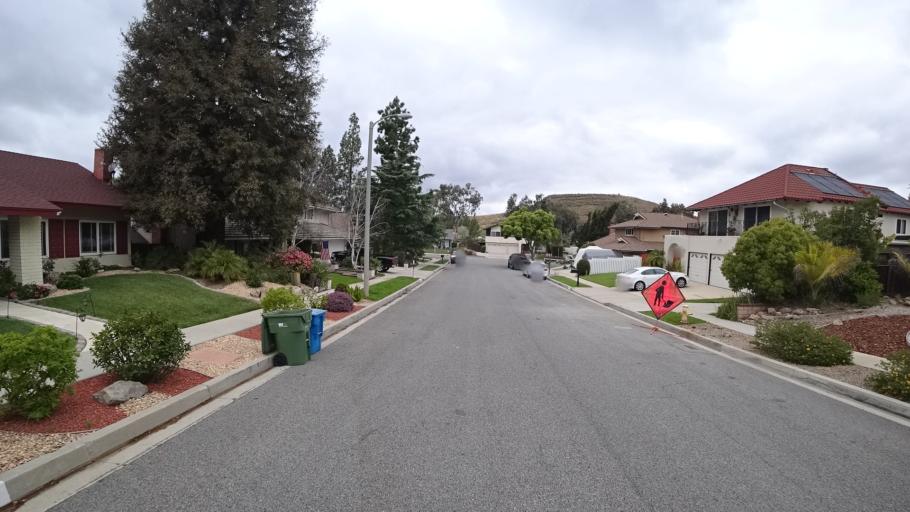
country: US
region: California
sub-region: Ventura County
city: Thousand Oaks
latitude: 34.2041
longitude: -118.8870
